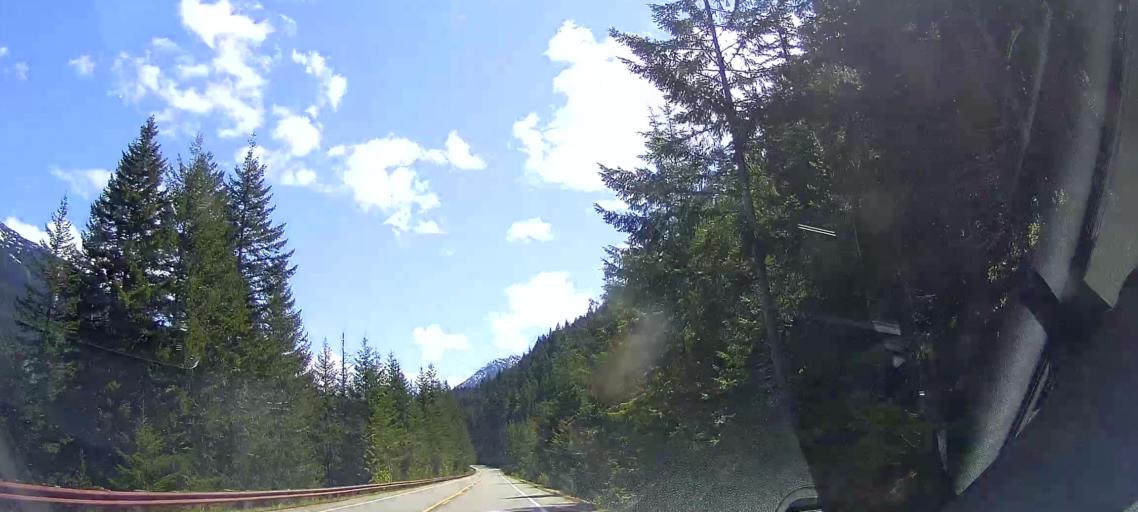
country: US
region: Washington
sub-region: Snohomish County
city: Darrington
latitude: 48.7269
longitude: -121.0363
